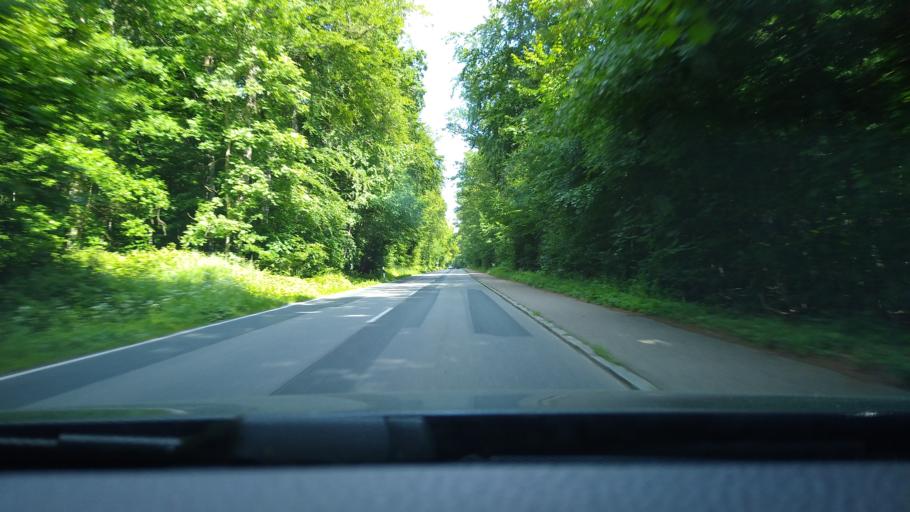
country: DE
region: Schleswig-Holstein
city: Kellenhusen
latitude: 54.1965
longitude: 11.0327
